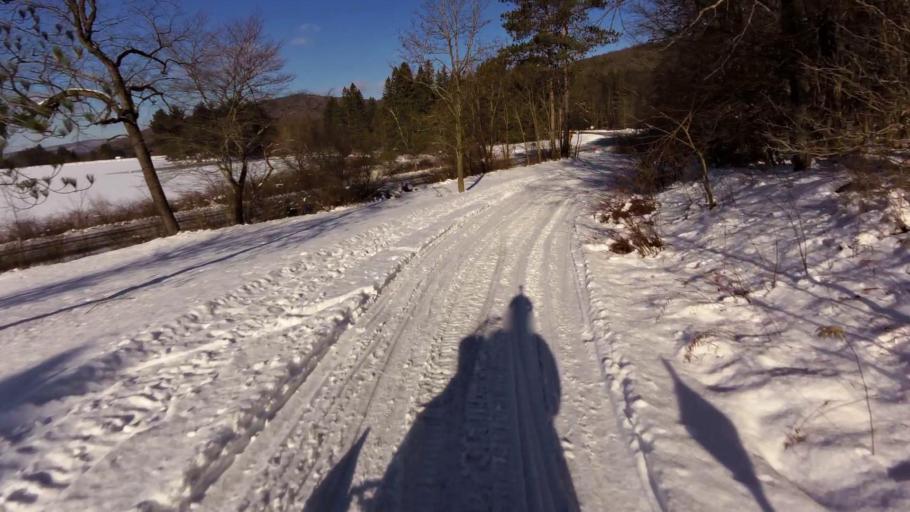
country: US
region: New York
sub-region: Cattaraugus County
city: Salamanca
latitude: 42.1049
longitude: -78.7422
